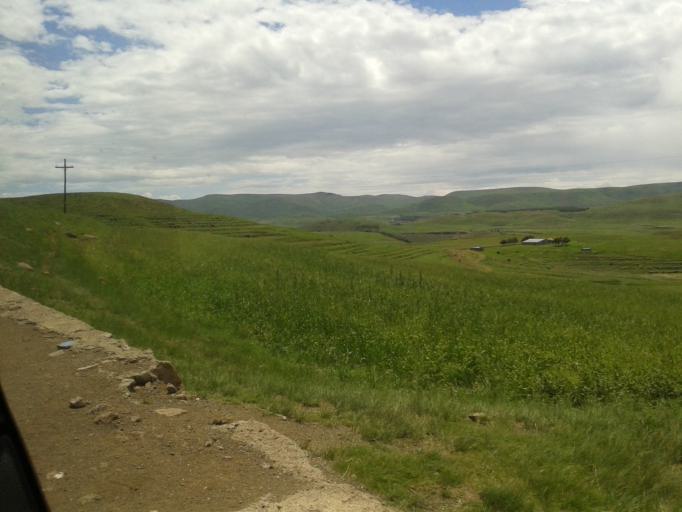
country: LS
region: Maseru
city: Nako
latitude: -29.8723
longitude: 28.0409
